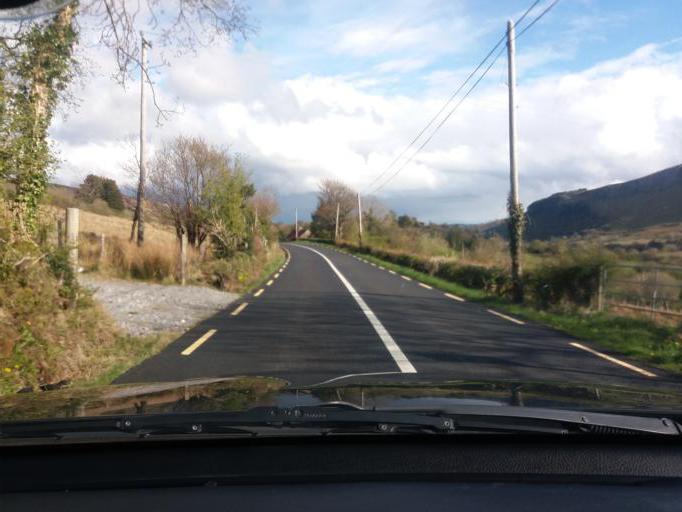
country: IE
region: Connaught
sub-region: County Leitrim
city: Kinlough
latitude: 54.3788
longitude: -8.2942
